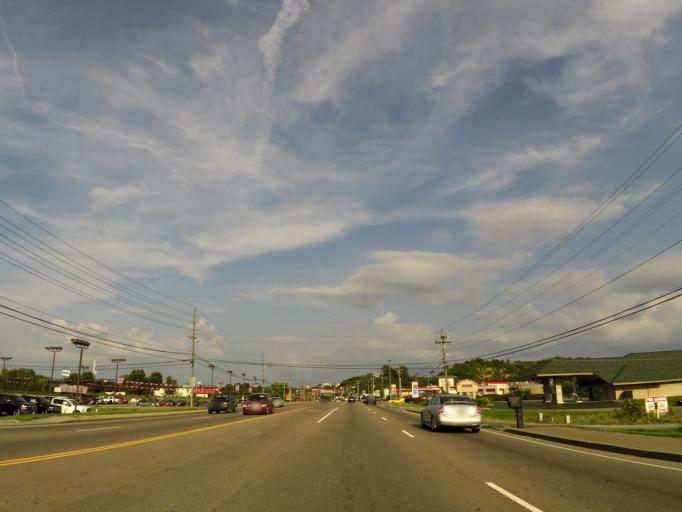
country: US
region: Tennessee
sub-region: Sevier County
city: Sevierville
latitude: 35.8650
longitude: -83.5487
